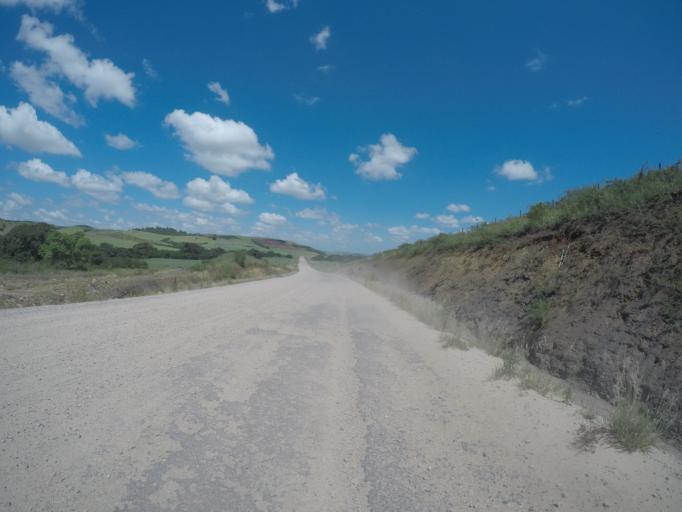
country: ZA
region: KwaZulu-Natal
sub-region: uThungulu District Municipality
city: Empangeni
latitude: -28.6402
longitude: 31.7643
